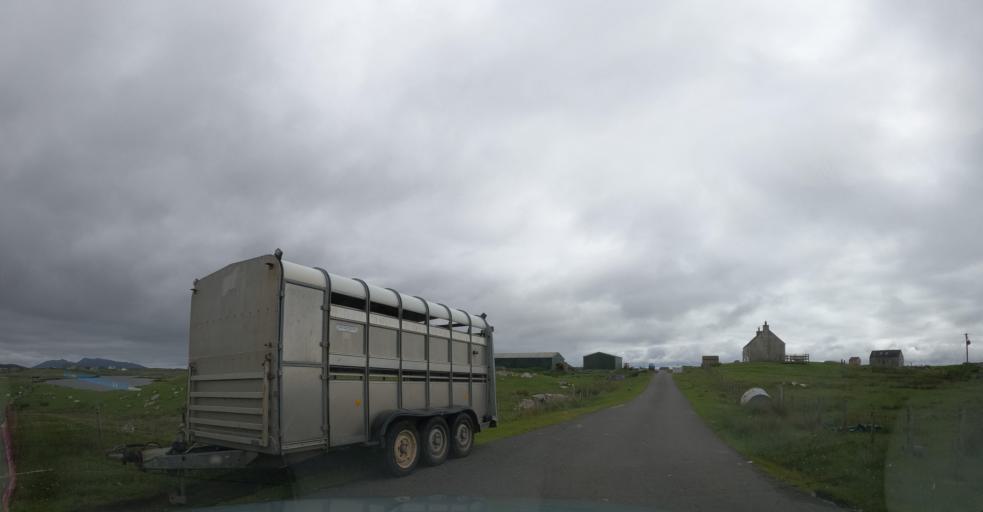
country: GB
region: Scotland
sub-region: Eilean Siar
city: Isle of North Uist
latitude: 57.5493
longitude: -7.3473
